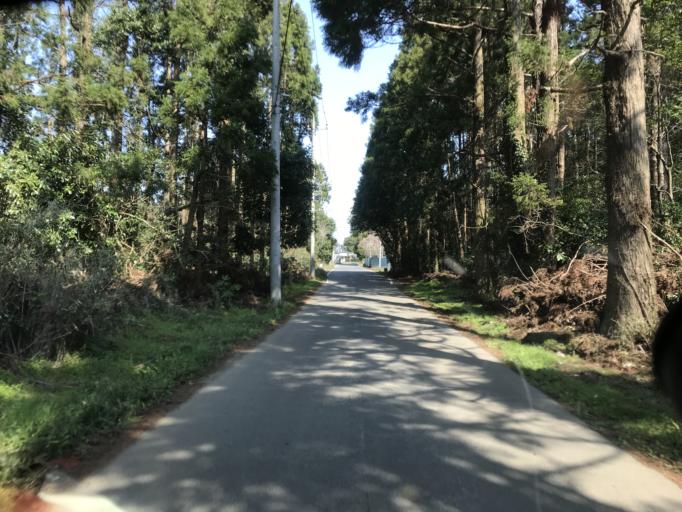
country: JP
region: Chiba
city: Sawara
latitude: 35.8433
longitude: 140.5250
